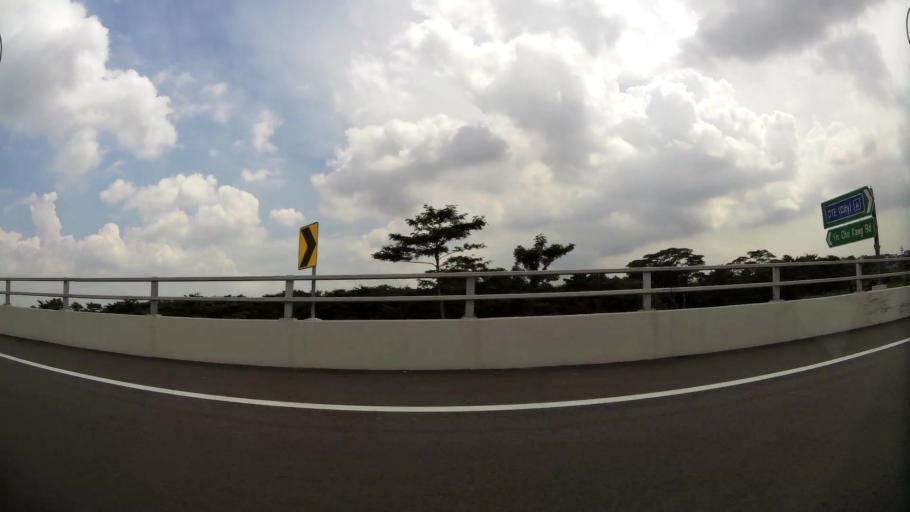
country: MY
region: Johor
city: Kampung Pasir Gudang Baru
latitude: 1.3986
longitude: 103.8577
